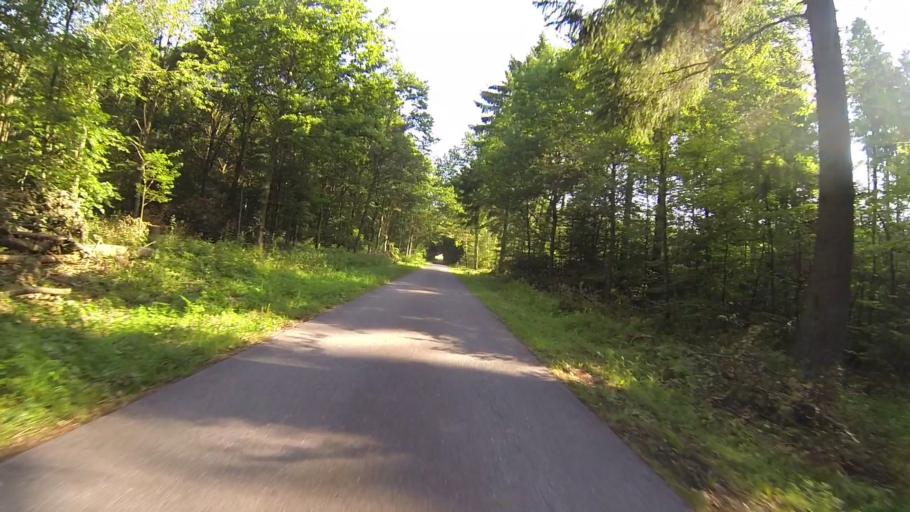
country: DE
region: Baden-Wuerttemberg
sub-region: Regierungsbezirk Stuttgart
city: Konigsbronn
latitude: 48.7227
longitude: 10.1128
